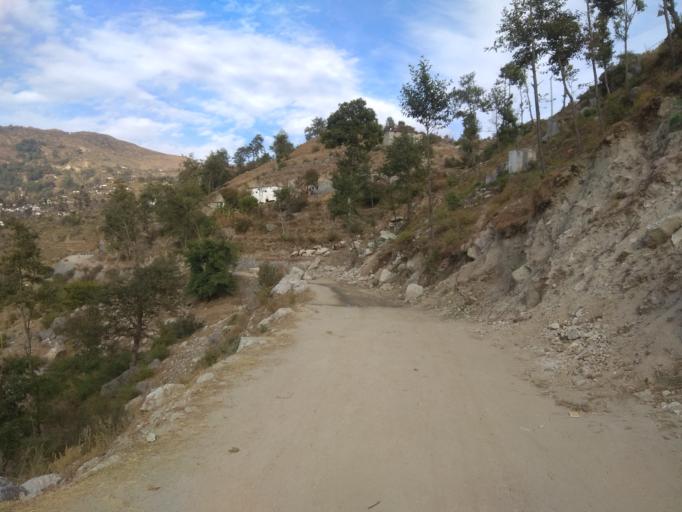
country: NP
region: Far Western
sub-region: Seti Zone
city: Achham
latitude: 29.2396
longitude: 81.6384
